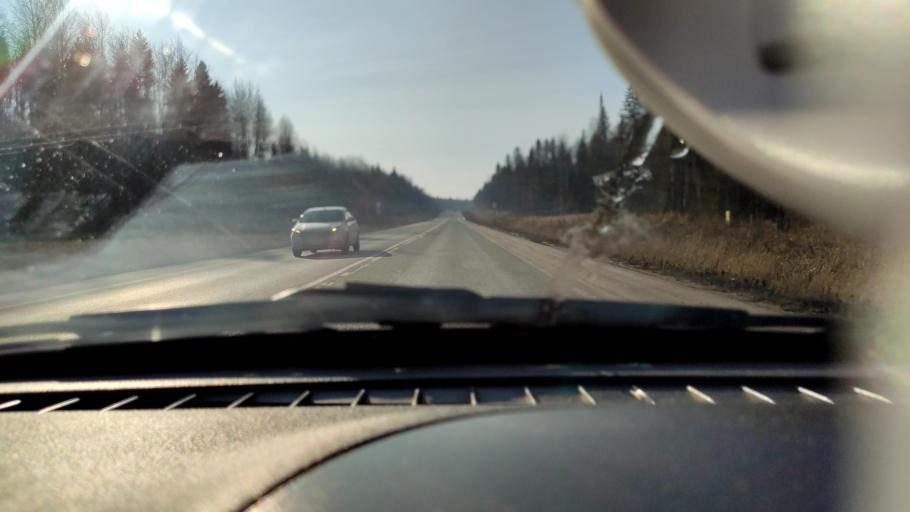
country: RU
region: Perm
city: Novyye Lyady
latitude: 58.0449
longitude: 56.5445
